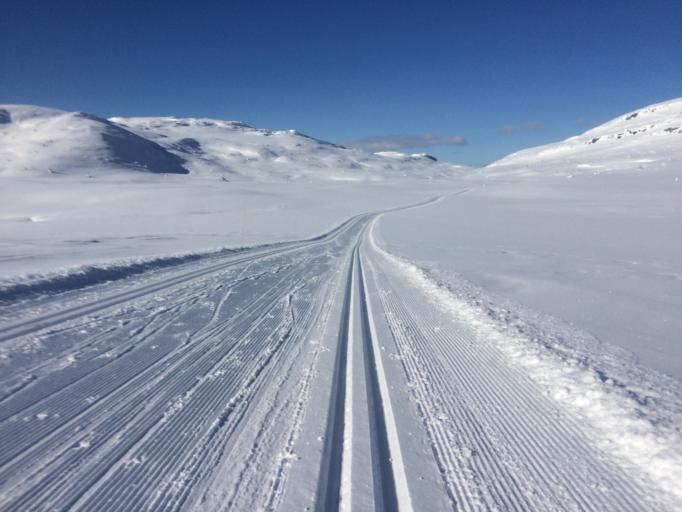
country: NO
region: Oppland
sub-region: Ringebu
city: Ringebu
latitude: 61.3795
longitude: 10.0609
